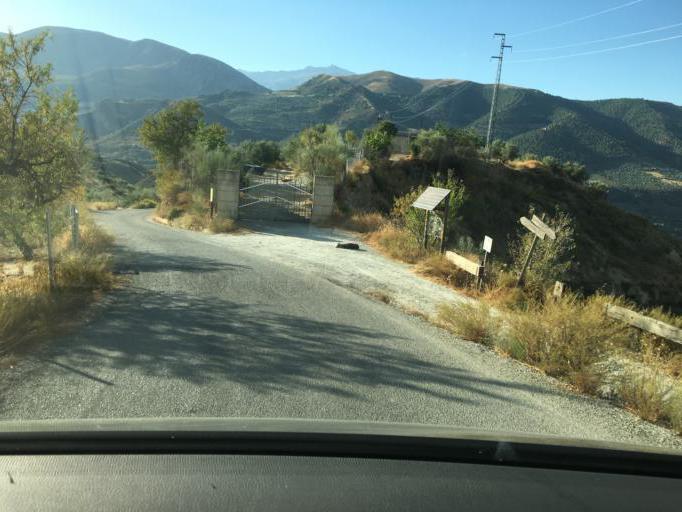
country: ES
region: Andalusia
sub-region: Provincia de Granada
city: Quentar
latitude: 37.2029
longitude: -3.4722
